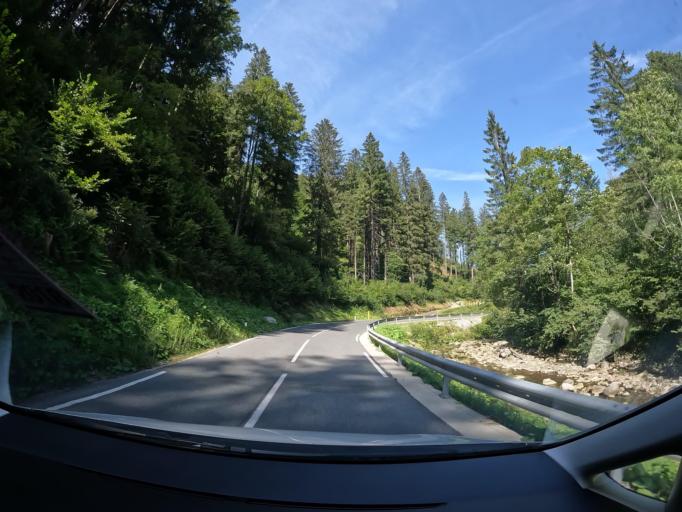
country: SI
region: Zirovnica
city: Zirovnica
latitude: 46.4425
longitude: 14.1675
